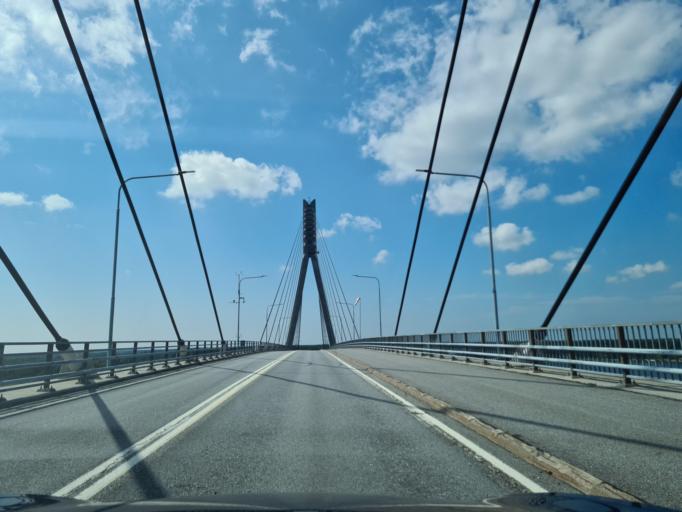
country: FI
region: Ostrobothnia
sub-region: Vaasa
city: Replot
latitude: 63.2066
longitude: 21.4746
